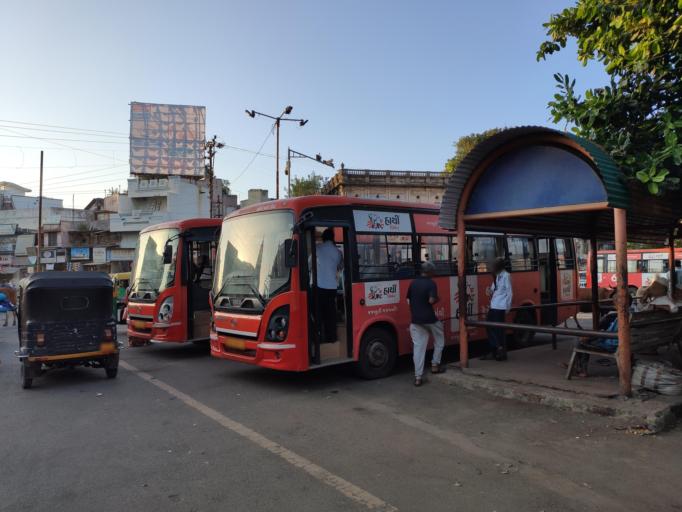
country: IN
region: Gujarat
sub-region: Jamnagar
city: Jamnagar
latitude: 22.4643
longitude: 70.0798
